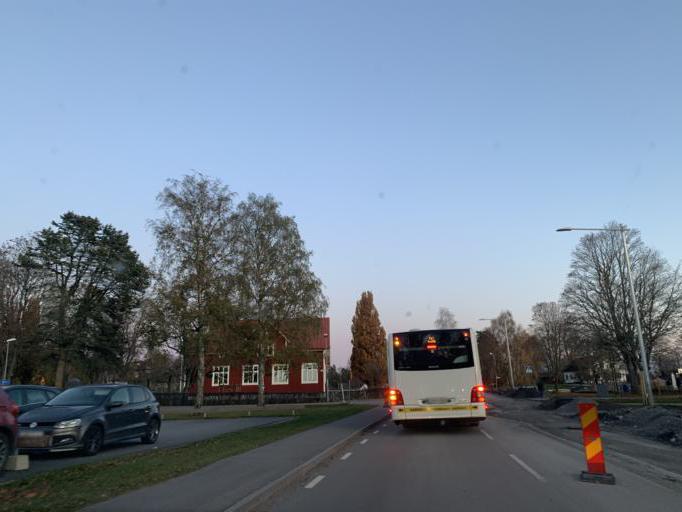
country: SE
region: OErebro
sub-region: Lindesbergs Kommun
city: Frovi
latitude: 59.3186
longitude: 15.3998
